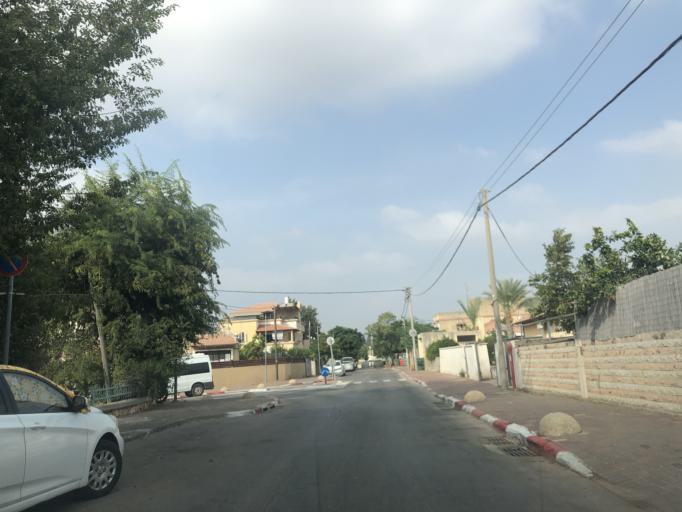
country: IL
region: Central District
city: Rosh Ha'Ayin
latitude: 32.0974
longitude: 34.9527
